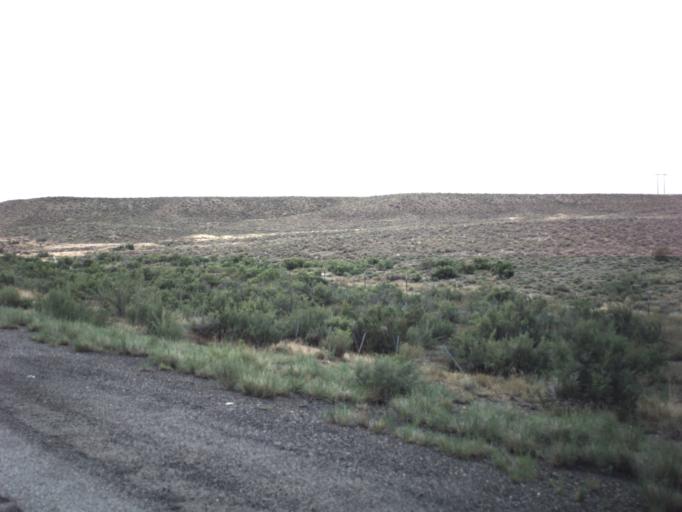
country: US
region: Utah
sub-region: Carbon County
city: Wellington
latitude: 39.5415
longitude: -110.6102
